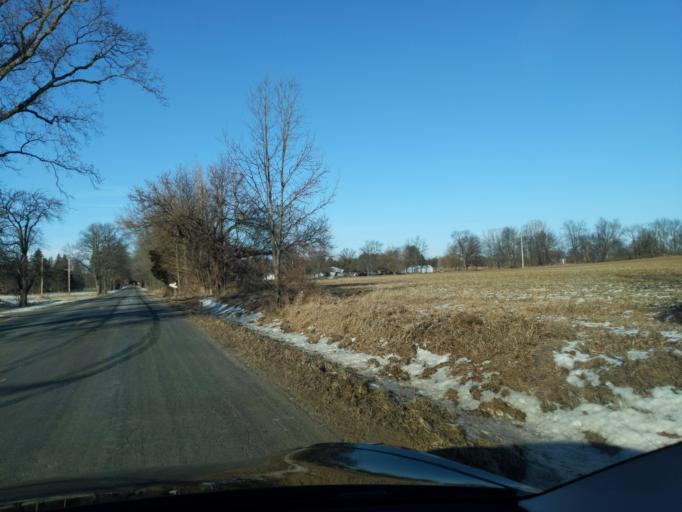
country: US
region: Michigan
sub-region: Ingham County
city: Stockbridge
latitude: 42.4480
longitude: -84.1506
